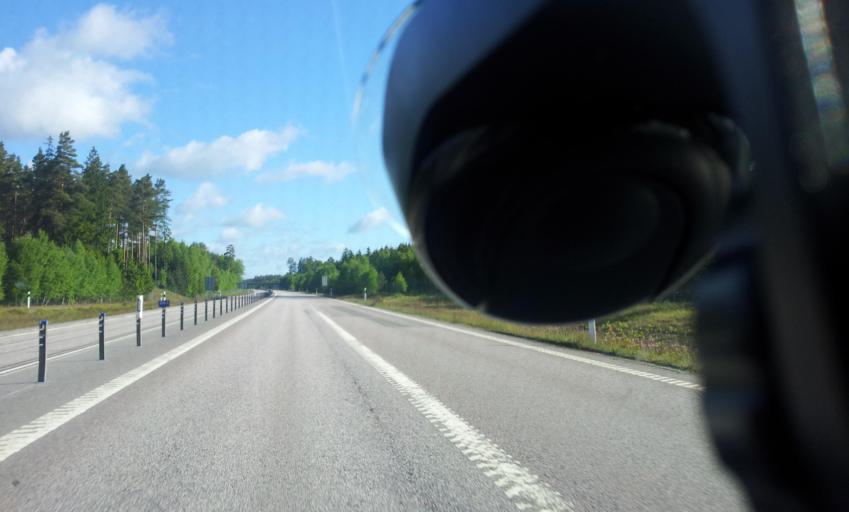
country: SE
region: Kalmar
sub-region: Torsas Kommun
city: Torsas
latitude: 56.5043
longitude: 16.0864
